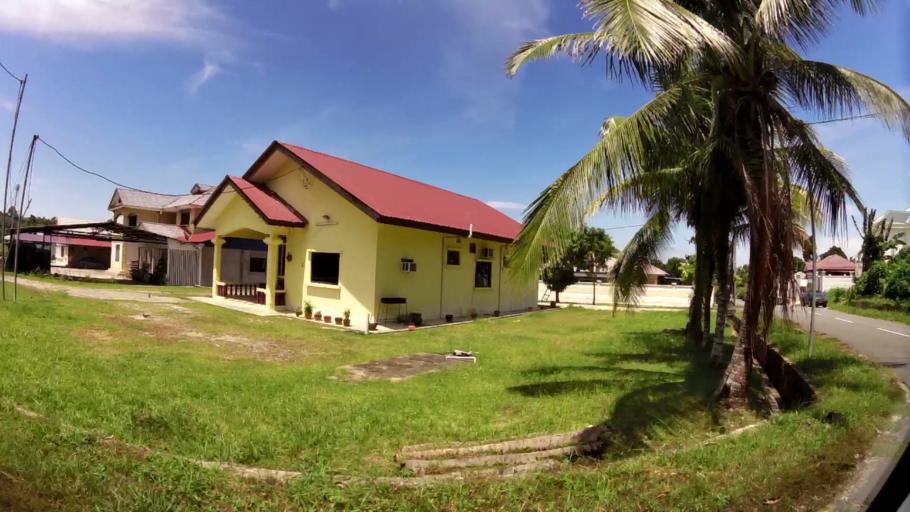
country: BN
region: Brunei and Muara
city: Bandar Seri Begawan
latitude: 4.9373
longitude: 114.9551
